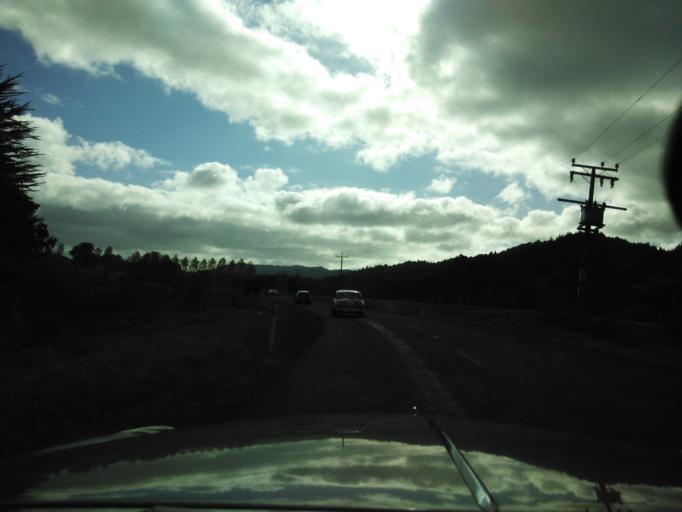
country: NZ
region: Auckland
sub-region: Auckland
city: Red Hill
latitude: -37.0905
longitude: 175.0907
